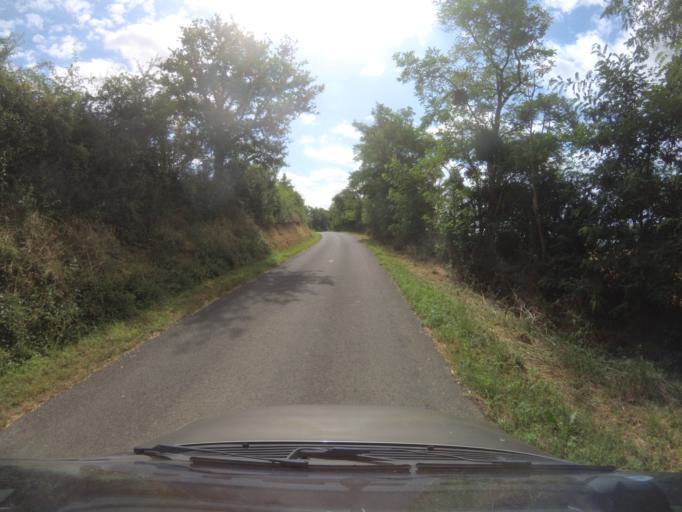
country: FR
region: Pays de la Loire
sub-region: Departement de Maine-et-Loire
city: Nueil-sur-Layon
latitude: 47.1800
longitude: -0.3502
